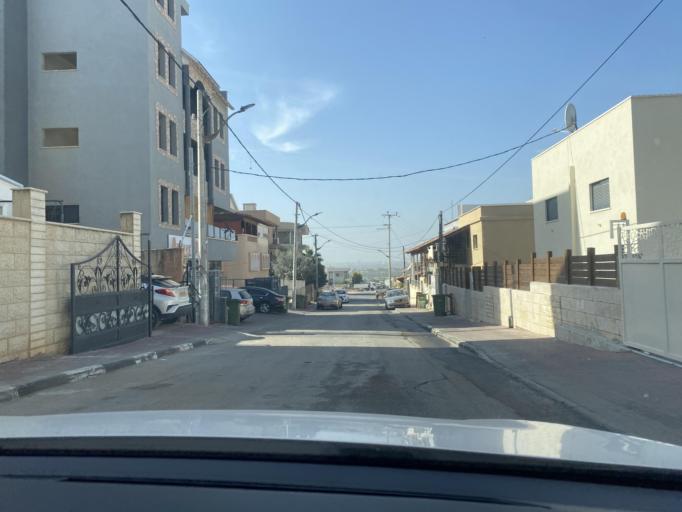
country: IL
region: Central District
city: Kafr Qasim
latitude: 32.1321
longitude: 34.9686
